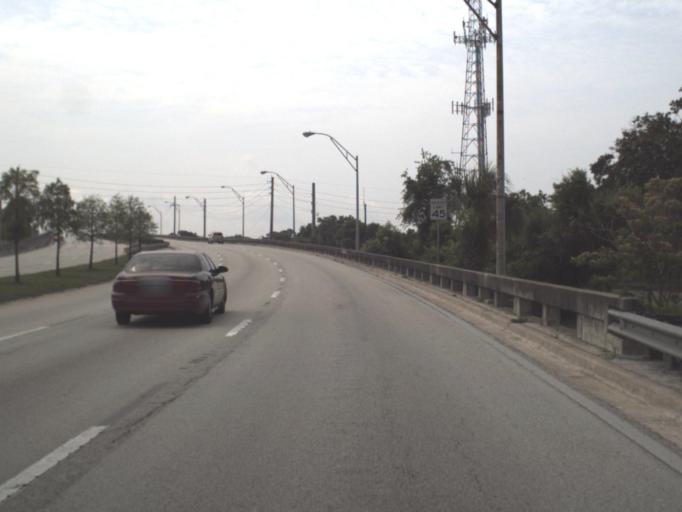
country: US
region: Florida
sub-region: Duval County
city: Jacksonville
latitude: 30.2766
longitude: -81.7197
